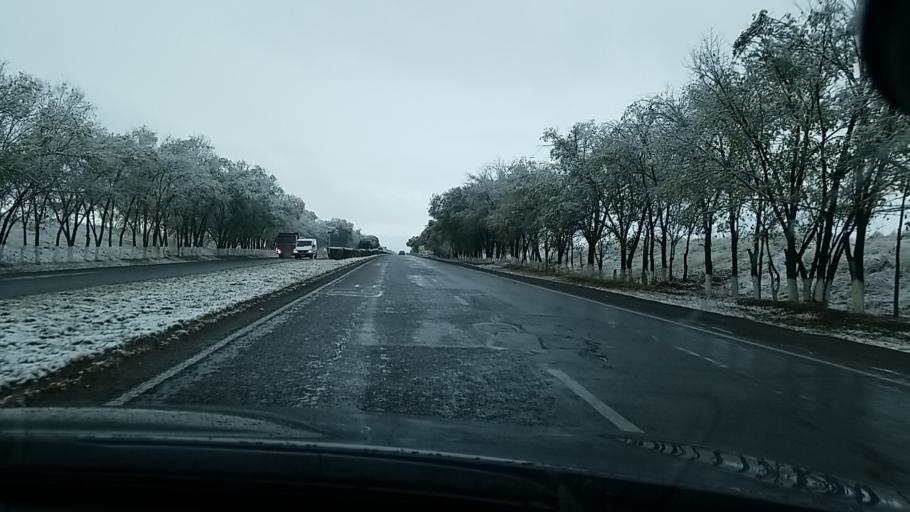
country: KZ
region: Almaty Oblysy
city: Burunday
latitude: 43.2208
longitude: 76.4547
